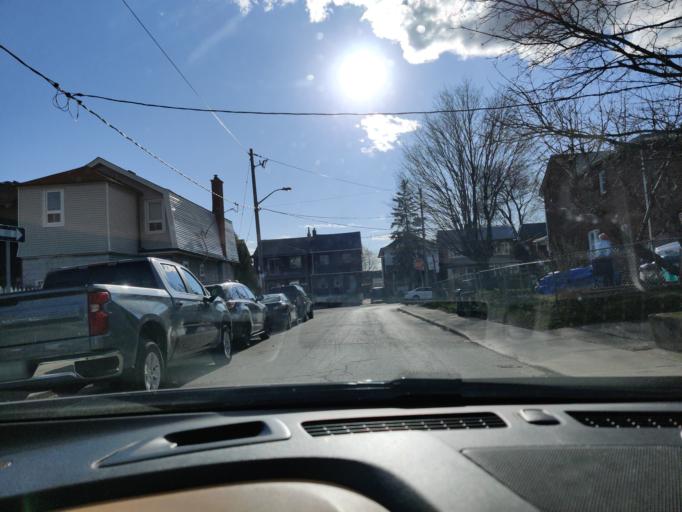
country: CA
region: Ontario
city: Toronto
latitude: 43.6900
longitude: -79.4425
